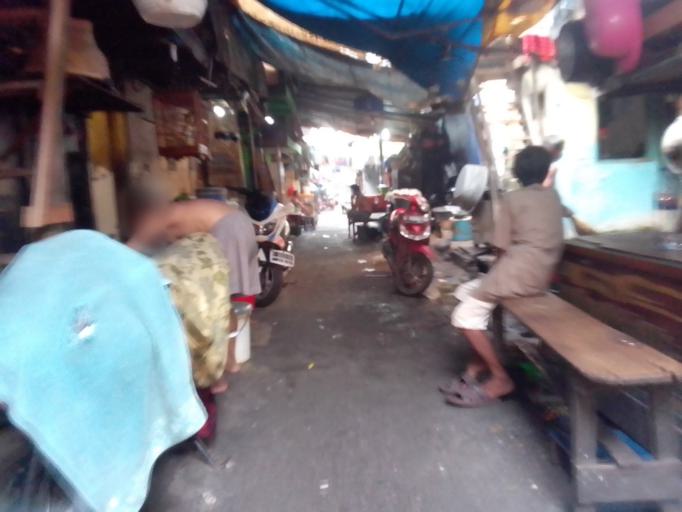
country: ID
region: Jakarta Raya
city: Jakarta
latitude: -6.1918
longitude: 106.8111
